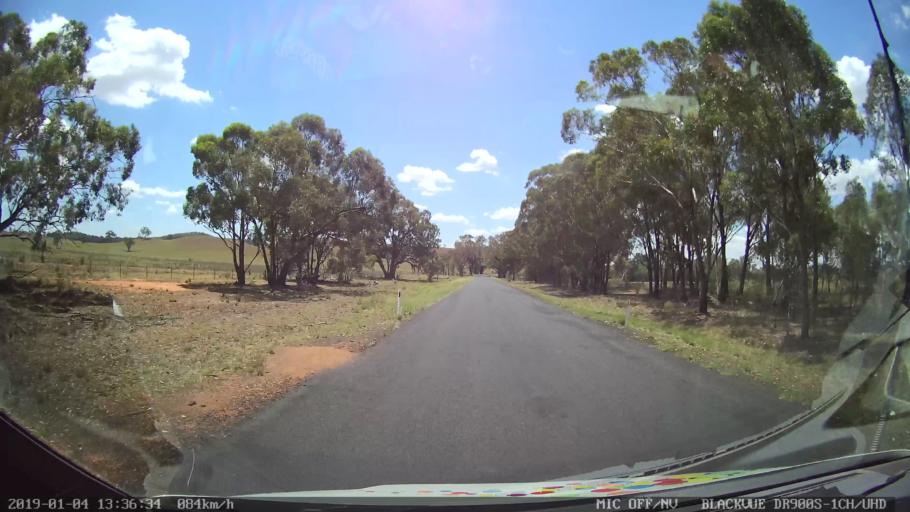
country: AU
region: New South Wales
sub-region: Dubbo Municipality
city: Dubbo
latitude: -32.5592
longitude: 148.5377
